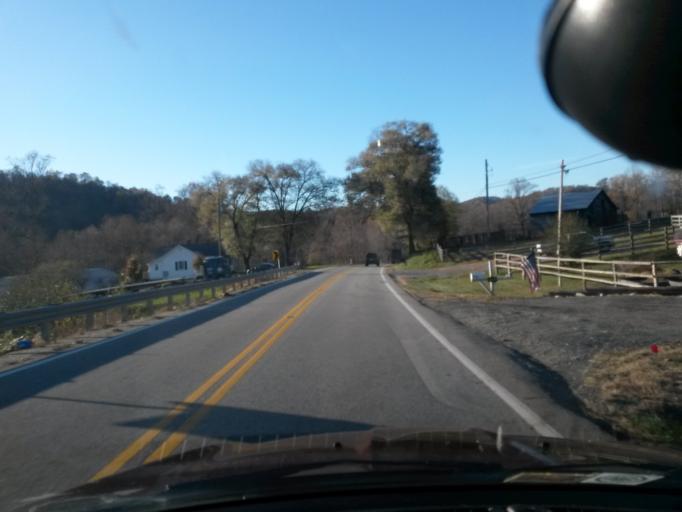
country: US
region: Virginia
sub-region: Amherst County
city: Amherst
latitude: 37.6239
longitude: -79.1137
